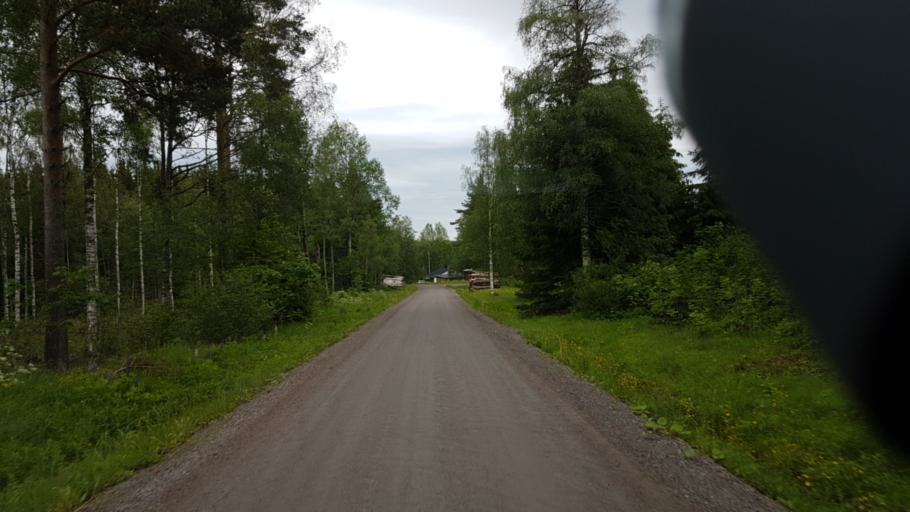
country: NO
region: Ostfold
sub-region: Romskog
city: Romskog
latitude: 59.7025
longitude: 12.0556
